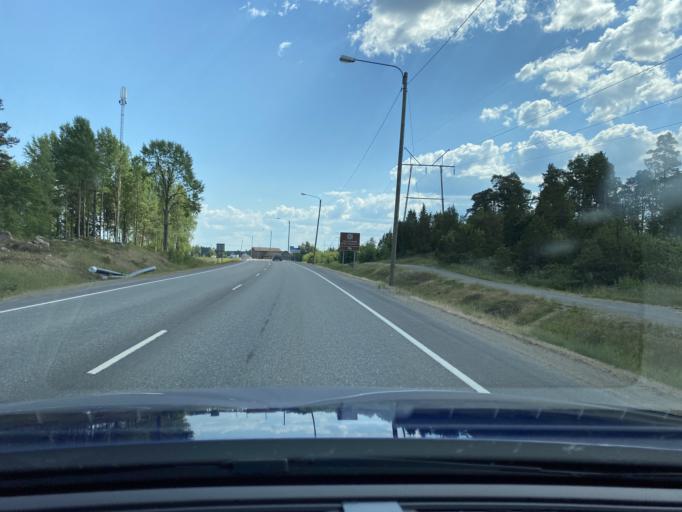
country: FI
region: Satakunta
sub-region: Rauma
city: Eura
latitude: 61.1261
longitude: 22.1273
